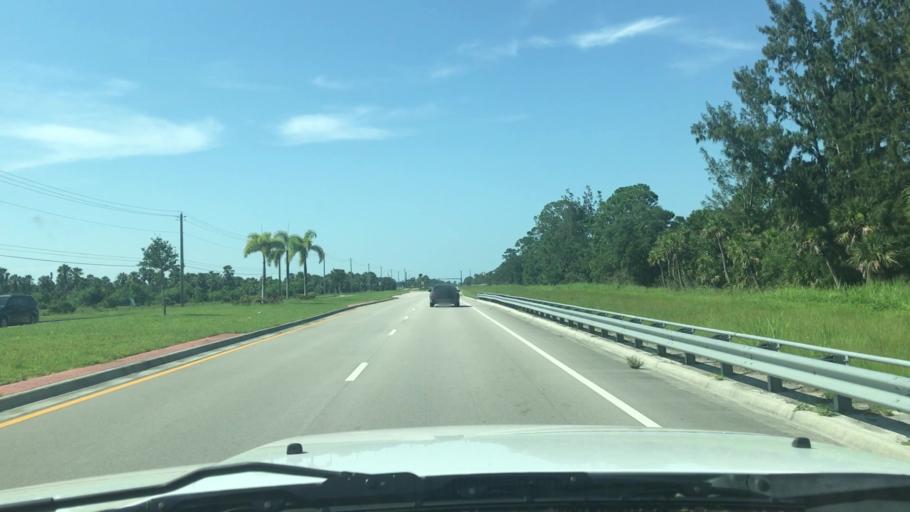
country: US
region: Florida
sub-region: Indian River County
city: West Vero Corridor
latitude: 27.6623
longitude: -80.4630
